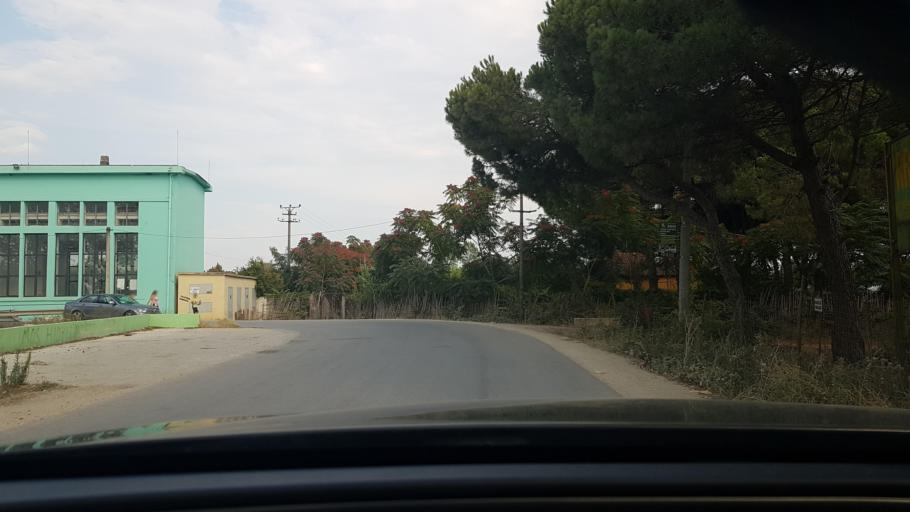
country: AL
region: Durres
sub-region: Rrethi i Durresit
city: Katundi i Ri
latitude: 41.4863
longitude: 19.5170
